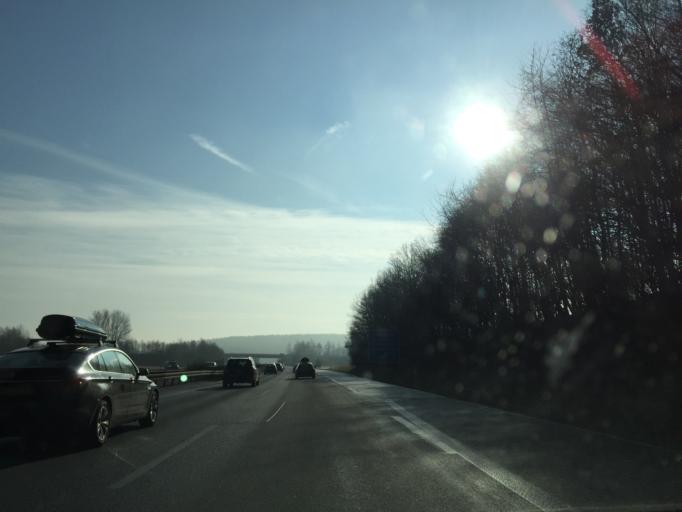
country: DE
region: Bavaria
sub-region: Upper Franconia
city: Schlusselfeld
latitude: 49.7457
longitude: 10.6276
